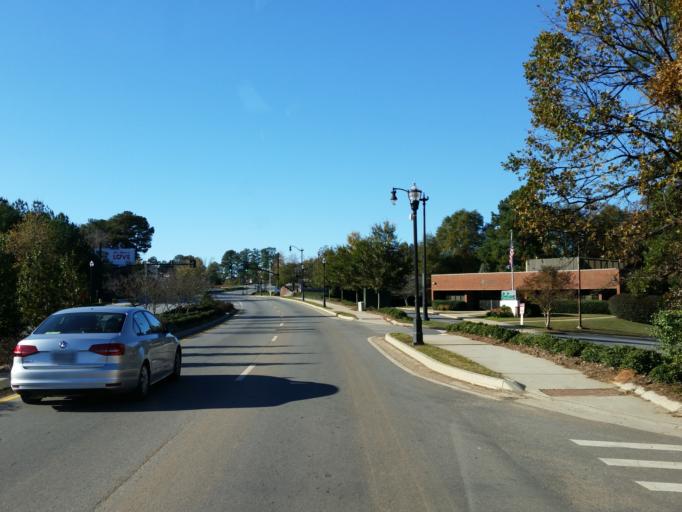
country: US
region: Georgia
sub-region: Cobb County
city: Fair Oaks
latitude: 33.9365
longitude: -84.5050
